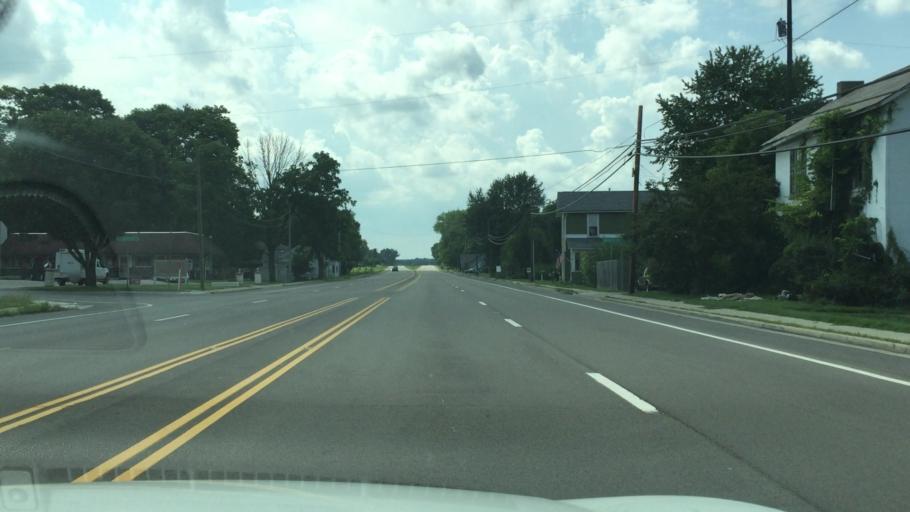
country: US
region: Ohio
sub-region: Clark County
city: Lisbon
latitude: 39.9239
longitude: -83.6964
